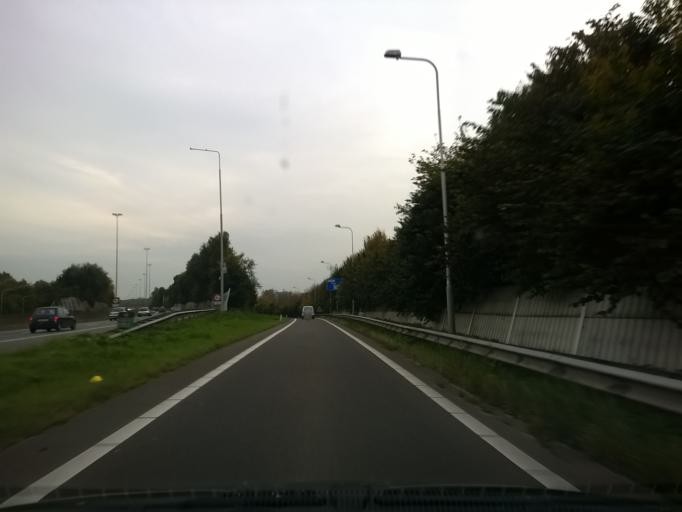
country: NL
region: Groningen
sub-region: Gemeente Groningen
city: Groningen
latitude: 53.1956
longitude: 6.5627
